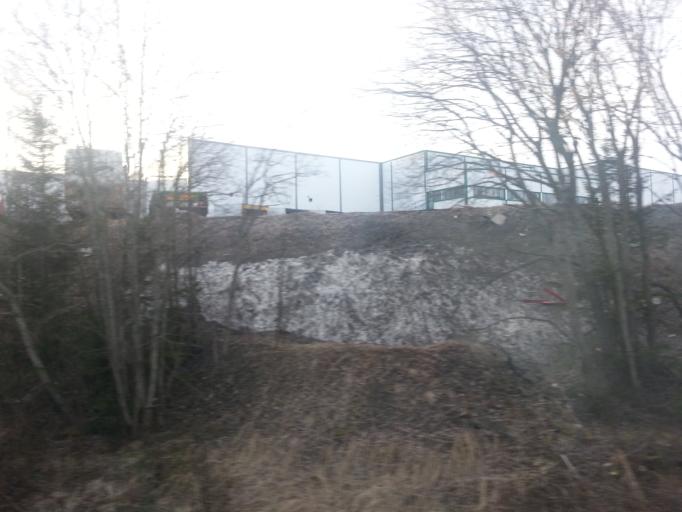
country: NO
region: Sor-Trondelag
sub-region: Trondheim
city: Trondheim
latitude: 63.3459
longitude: 10.3532
